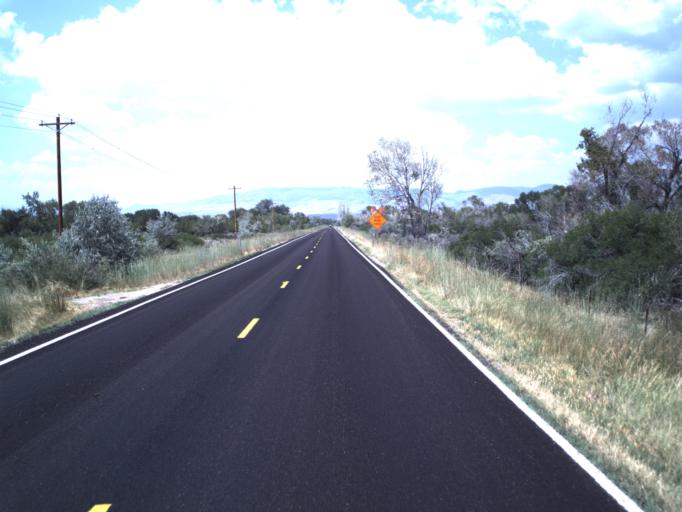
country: US
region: Utah
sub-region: Duchesne County
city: Roosevelt
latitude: 40.4208
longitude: -109.9218
